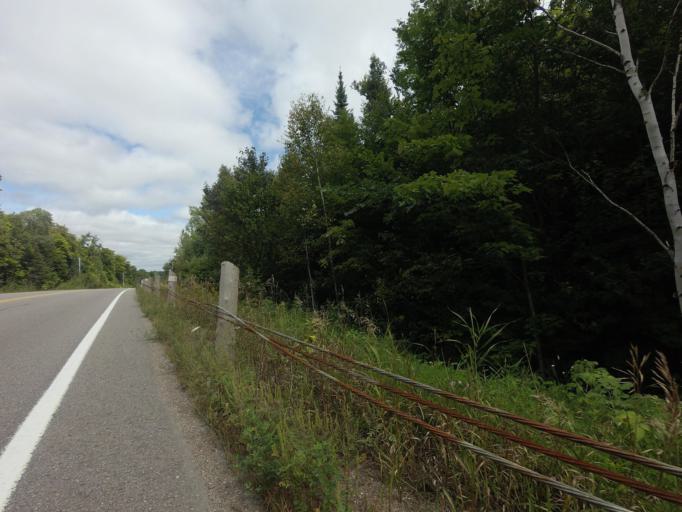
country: CA
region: Ontario
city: Omemee
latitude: 44.8575
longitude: -78.5461
